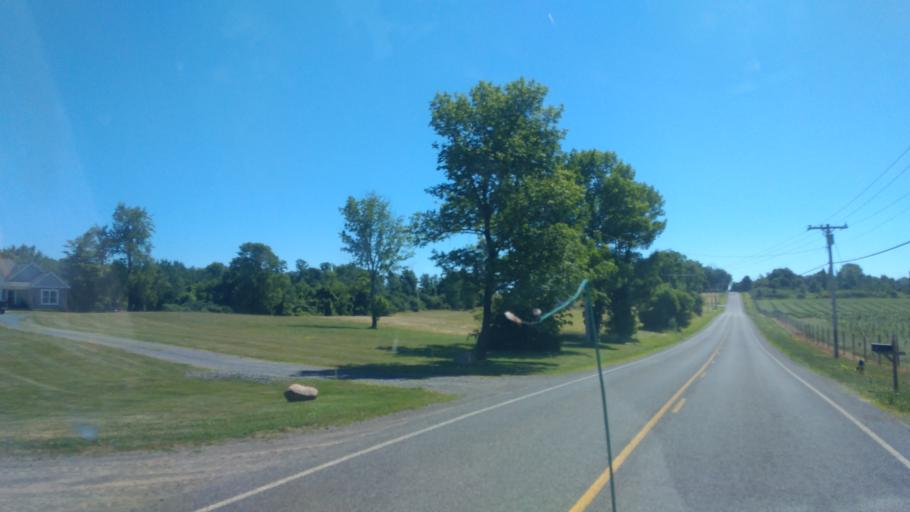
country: US
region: New York
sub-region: Wayne County
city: Sodus
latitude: 43.2731
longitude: -77.1048
